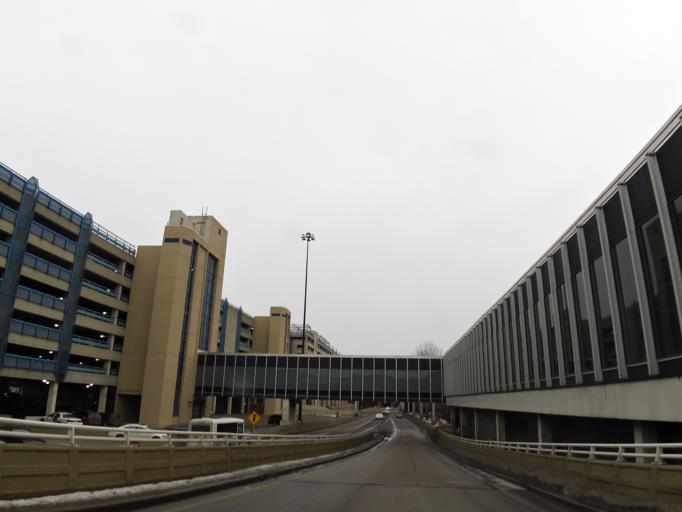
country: US
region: Minnesota
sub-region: Hennepin County
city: Richfield
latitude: 44.8819
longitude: -93.2110
